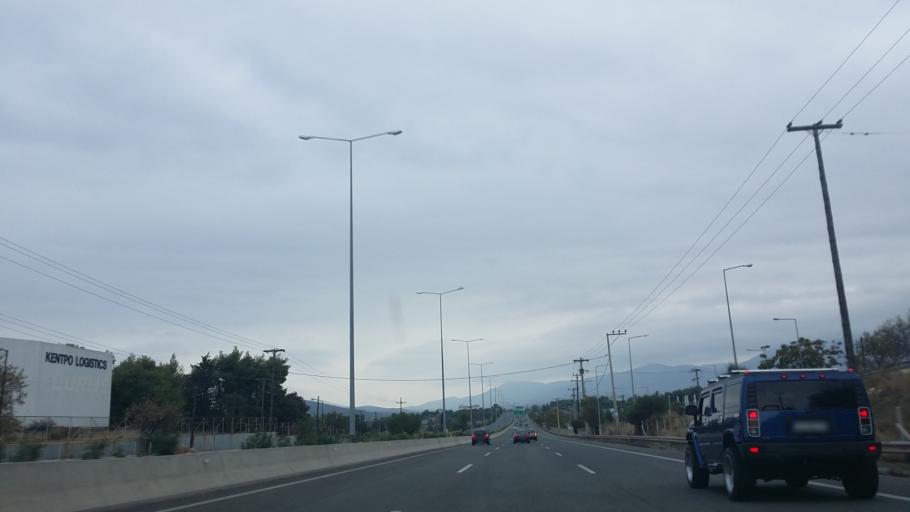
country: GR
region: Central Greece
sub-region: Nomos Voiotias
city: Oinofyta
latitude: 38.3013
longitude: 23.6570
